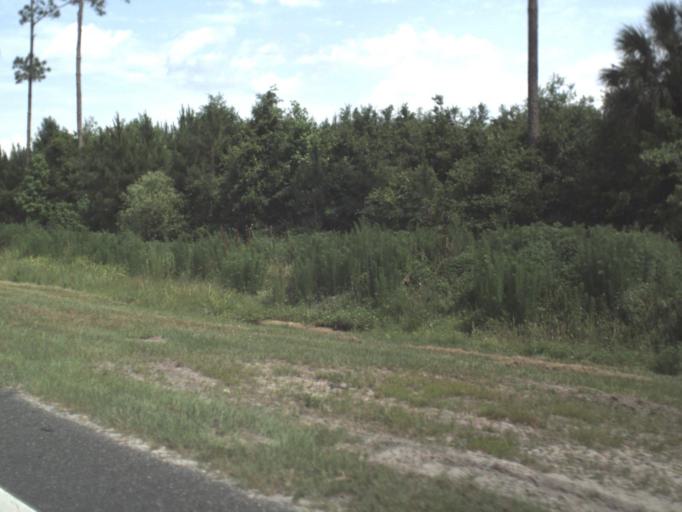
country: US
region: Florida
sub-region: Putnam County
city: Palatka
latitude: 29.6300
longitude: -81.7503
